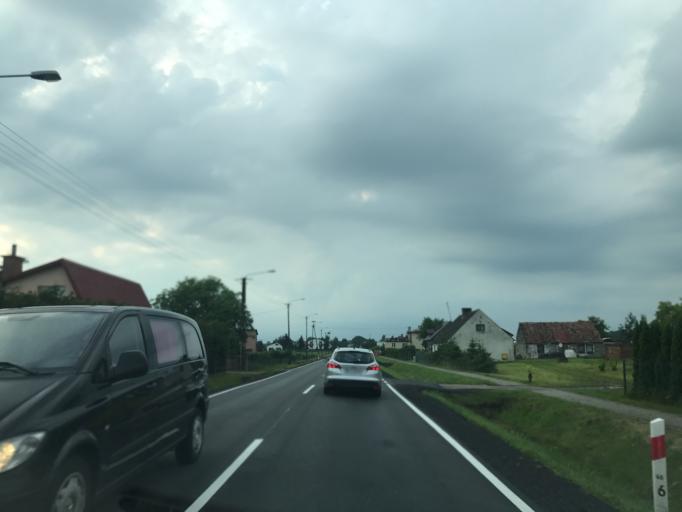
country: PL
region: Pomeranian Voivodeship
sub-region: Powiat czluchowski
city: Czluchow
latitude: 53.6808
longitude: 17.3370
